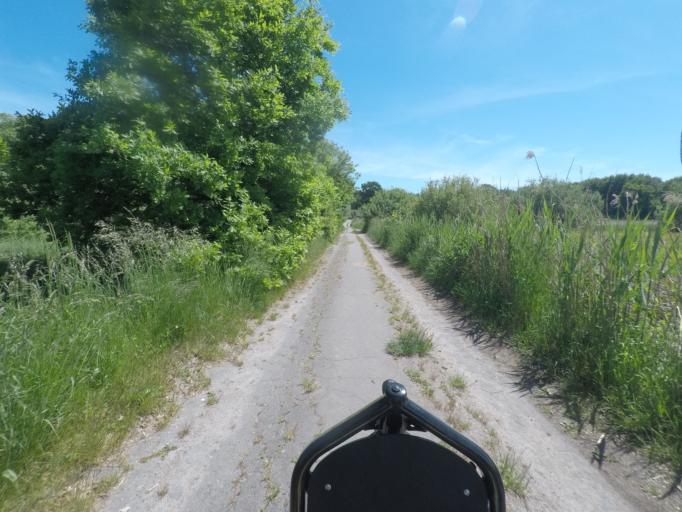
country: DE
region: Schleswig-Holstein
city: Stapelfeld
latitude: 53.6348
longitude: 10.1991
